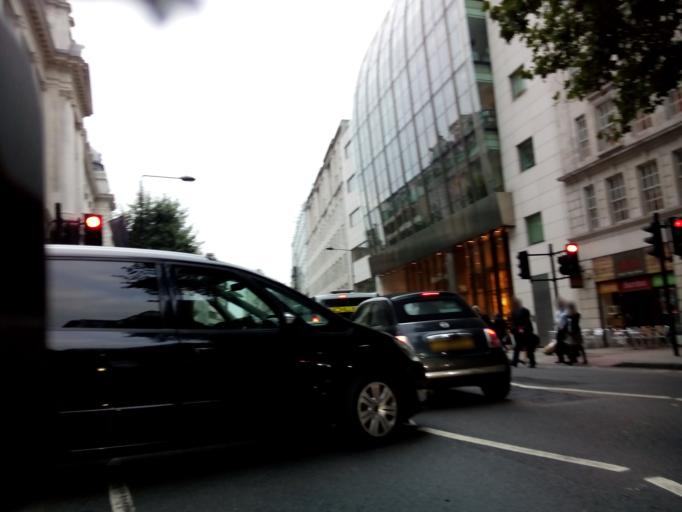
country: GB
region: England
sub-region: Greater London
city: Clerkenwell
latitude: 51.5179
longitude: -0.1172
